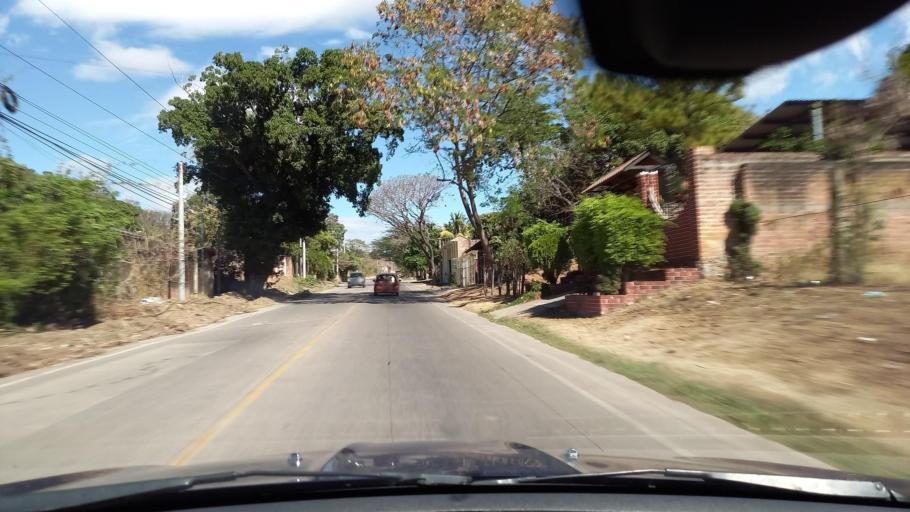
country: SV
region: Santa Ana
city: Metapan
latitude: 14.3542
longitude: -89.4541
